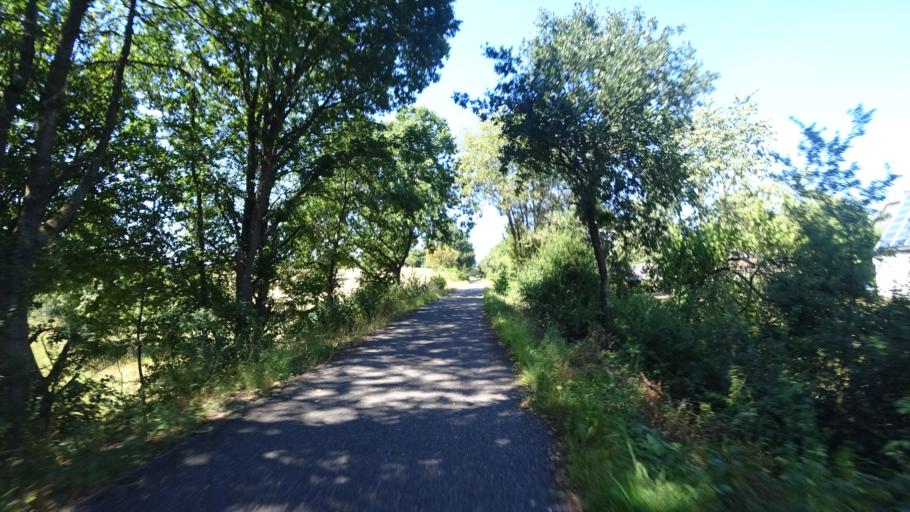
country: DE
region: Rheinland-Pfalz
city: Alterkulz
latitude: 50.0279
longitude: 7.4691
